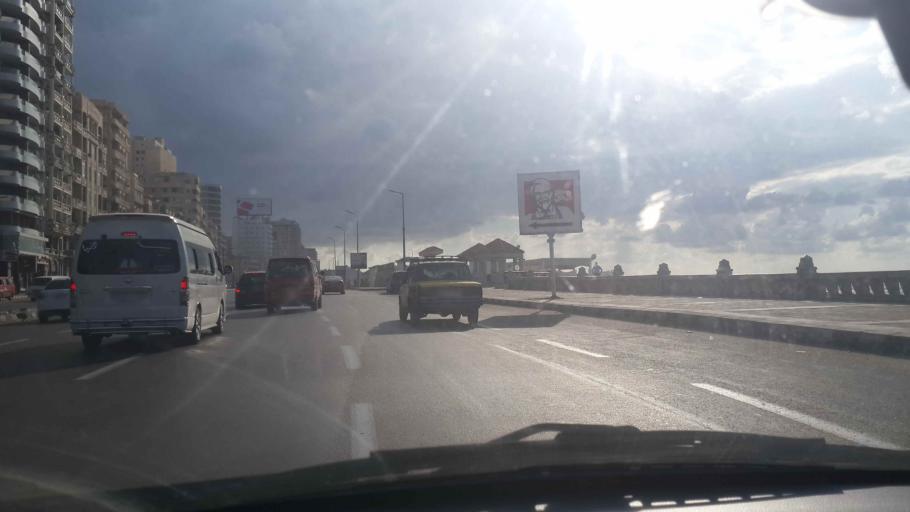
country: EG
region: Alexandria
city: Alexandria
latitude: 31.2194
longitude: 29.9280
